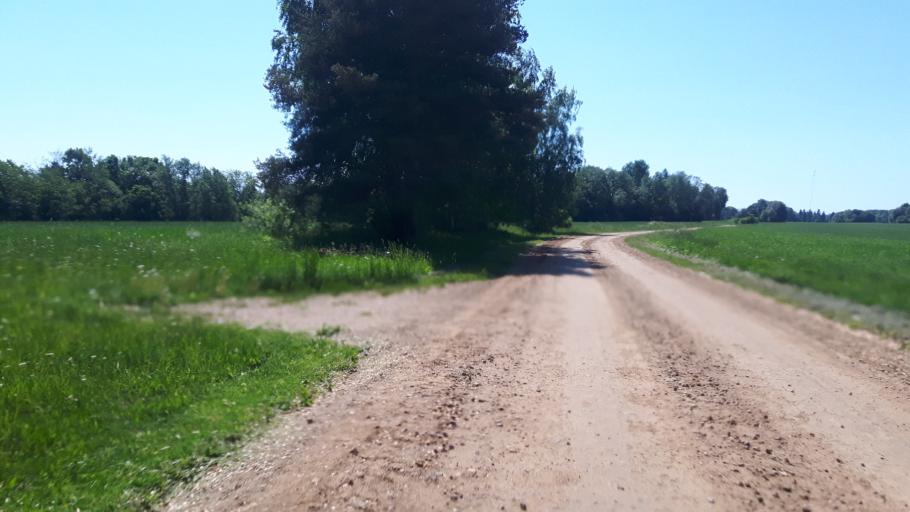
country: EE
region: Paernumaa
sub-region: Tootsi vald
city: Tootsi
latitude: 58.5028
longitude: 24.9060
